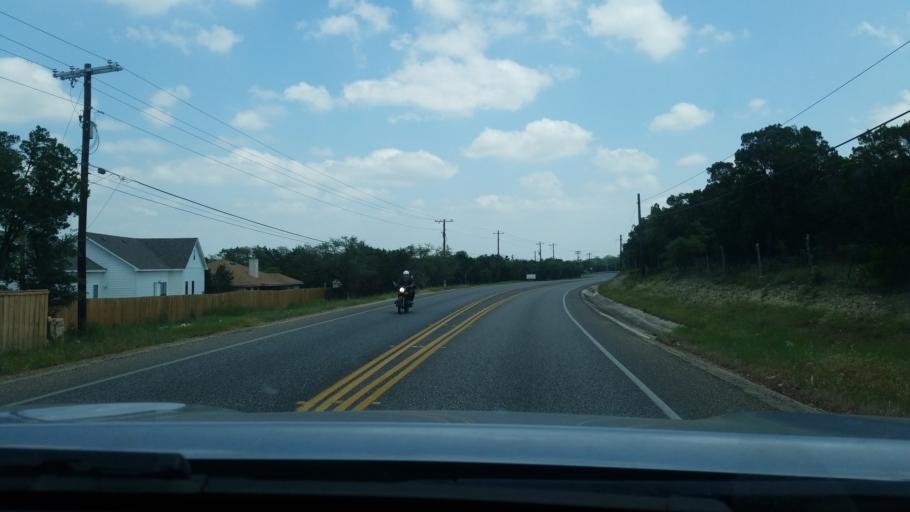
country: US
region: Texas
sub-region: Hays County
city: Woodcreek
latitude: 30.0159
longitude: -98.1251
